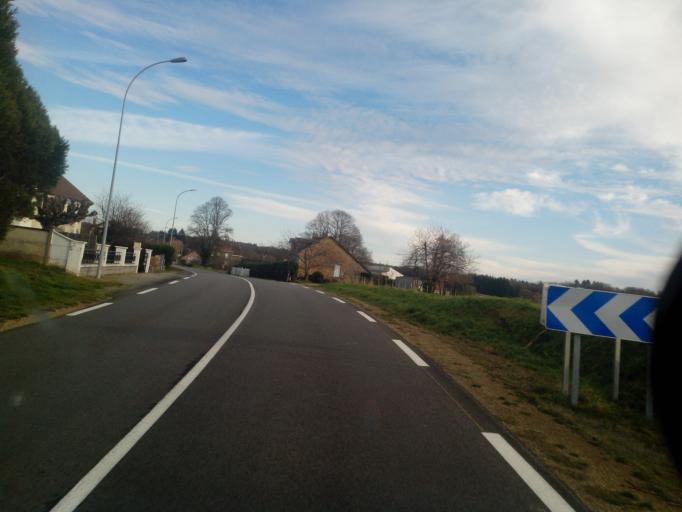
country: FR
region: Limousin
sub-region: Departement de la Haute-Vienne
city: Neuvic-Entier
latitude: 45.7310
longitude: 1.6178
